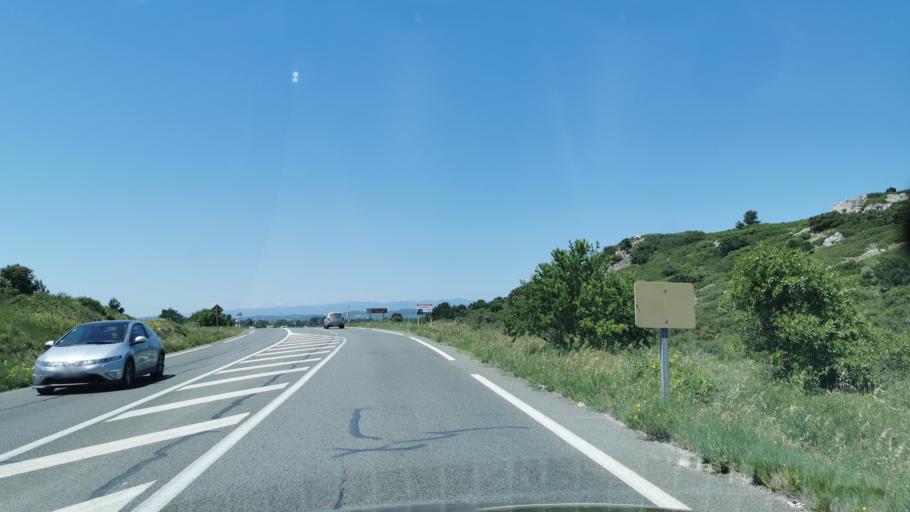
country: FR
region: Languedoc-Roussillon
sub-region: Departement de l'Aude
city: Nevian
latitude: 43.2064
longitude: 2.8852
